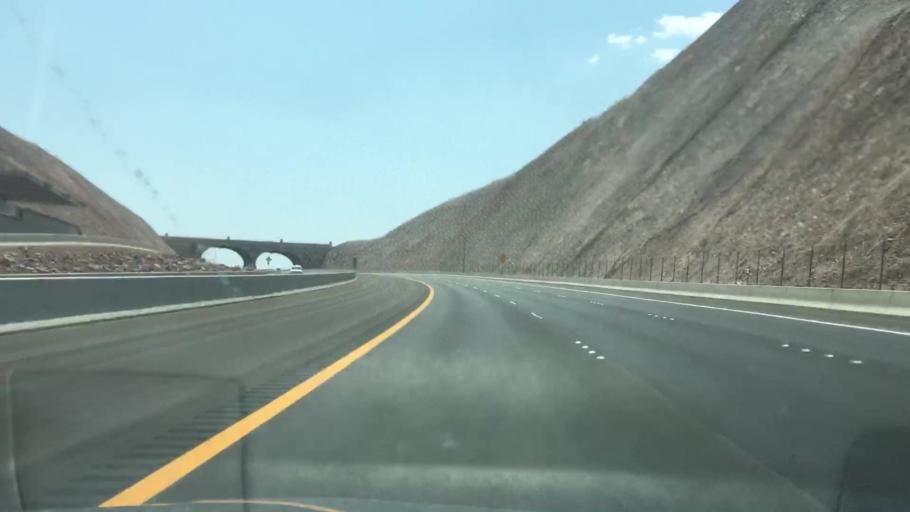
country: US
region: Nevada
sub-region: Clark County
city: Boulder City
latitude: 35.9959
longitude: -114.7998
